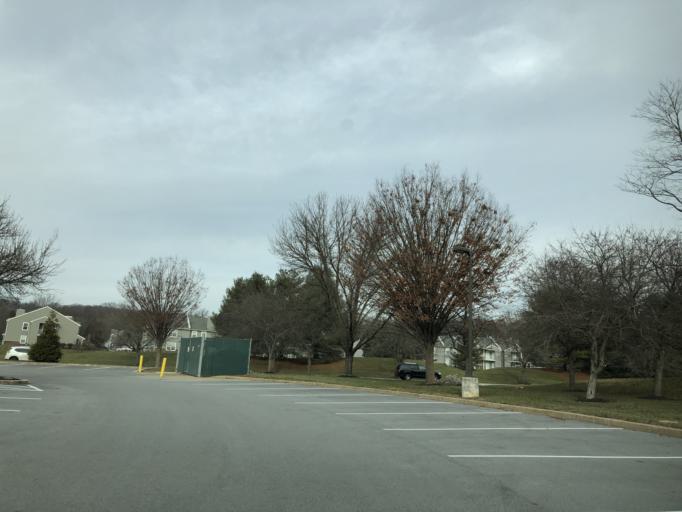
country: US
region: Pennsylvania
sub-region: Chester County
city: Exton
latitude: 40.0276
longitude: -75.6402
